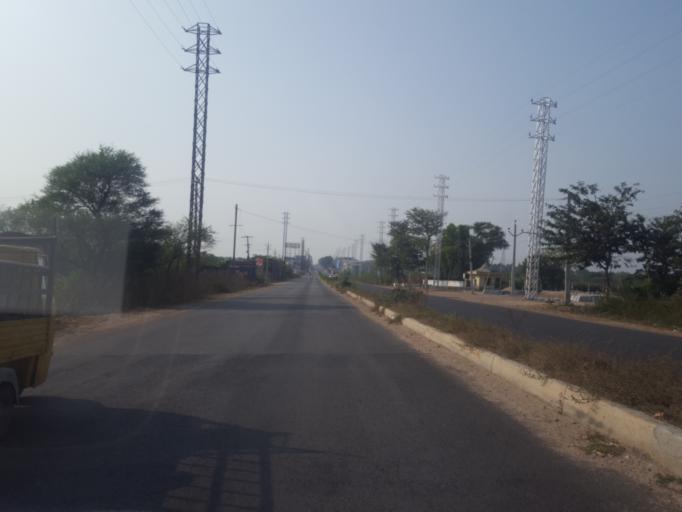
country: IN
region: Telangana
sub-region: Medak
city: Serilingampalle
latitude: 17.4023
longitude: 78.2911
